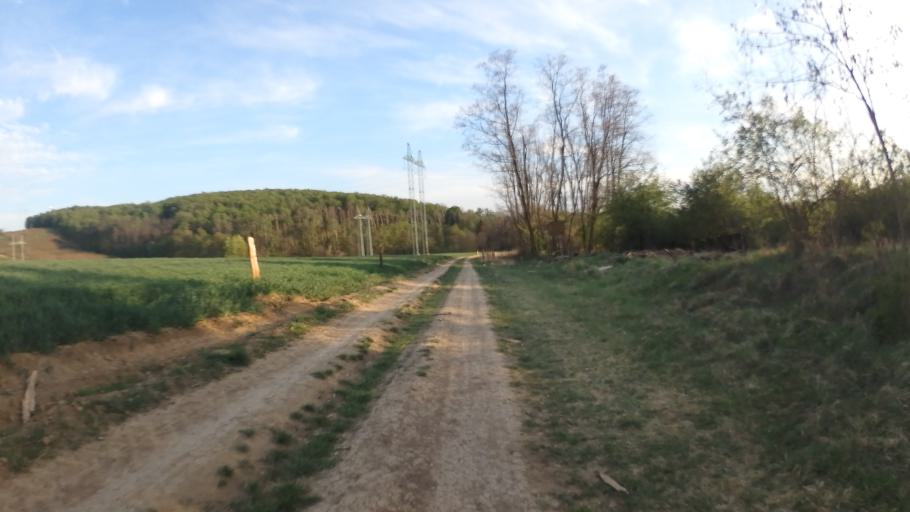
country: CZ
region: South Moravian
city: Moravany
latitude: 49.1375
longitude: 16.5617
